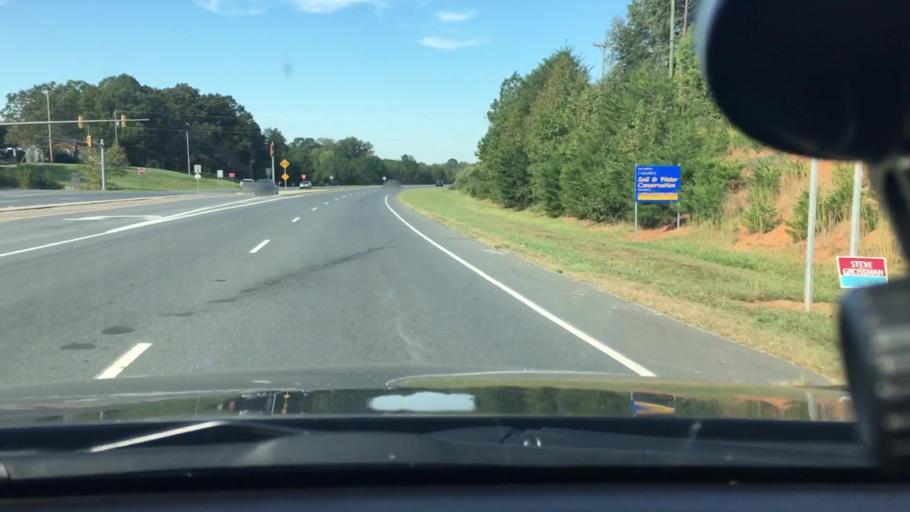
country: US
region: North Carolina
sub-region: Stanly County
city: Locust
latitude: 35.2539
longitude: -80.4612
